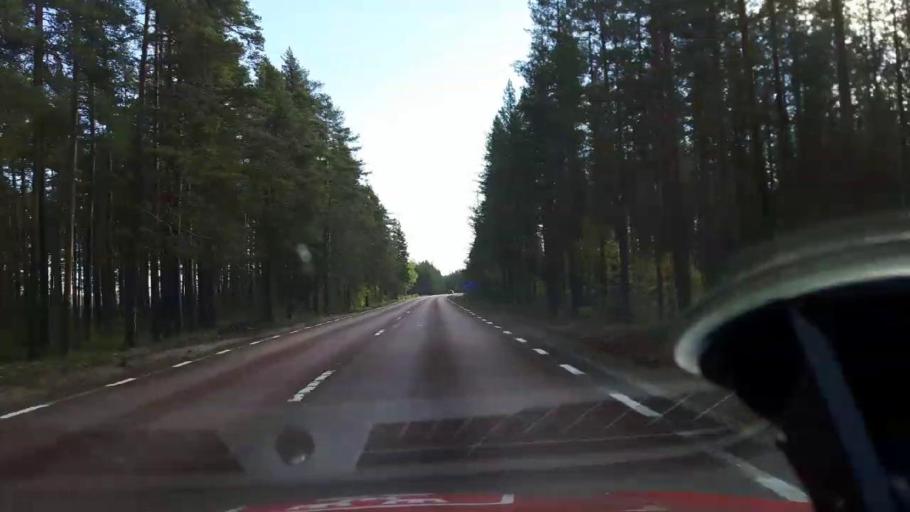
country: SE
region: Gaevleborg
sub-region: Ljusdals Kommun
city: Farila
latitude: 61.9371
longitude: 15.5091
